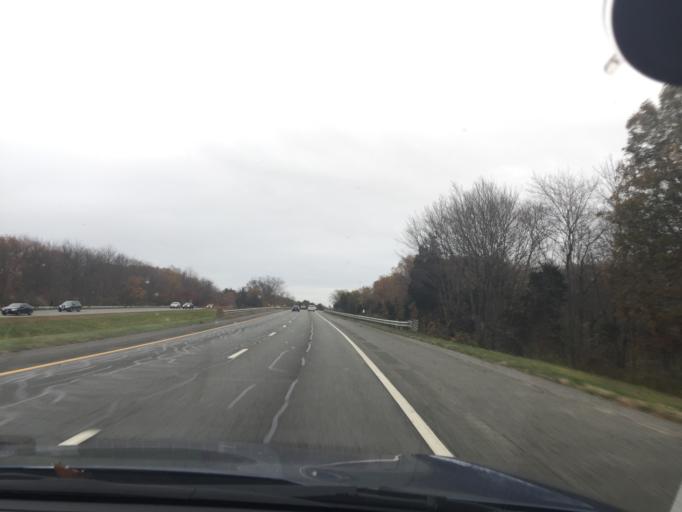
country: US
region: Rhode Island
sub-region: Providence County
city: Johnston
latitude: 41.7768
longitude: -71.4966
